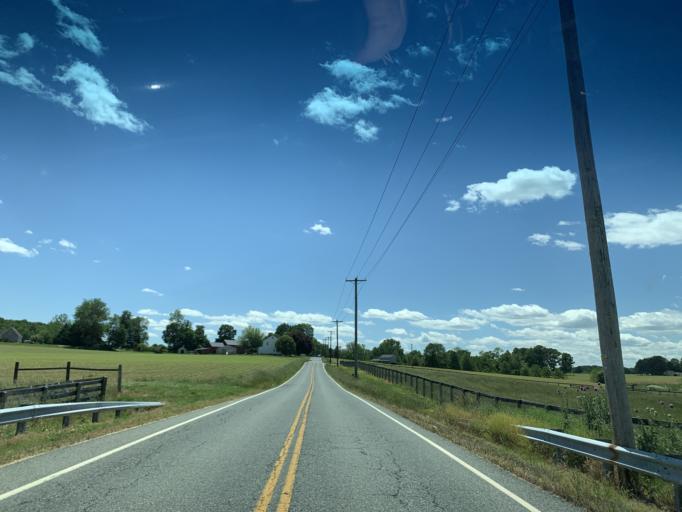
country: US
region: Maryland
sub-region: Cecil County
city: Rising Sun
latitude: 39.6828
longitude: -76.0140
